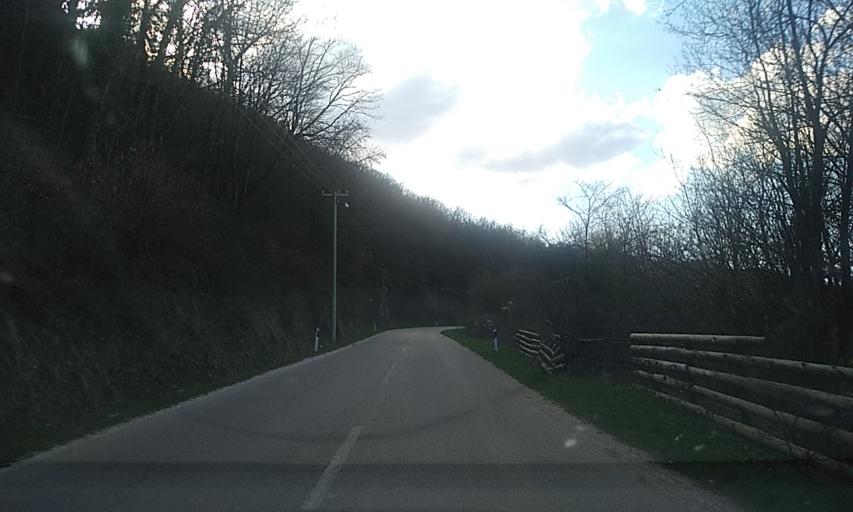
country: RS
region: Central Serbia
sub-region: Pcinjski Okrug
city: Bosilegrad
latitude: 42.4649
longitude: 22.4870
